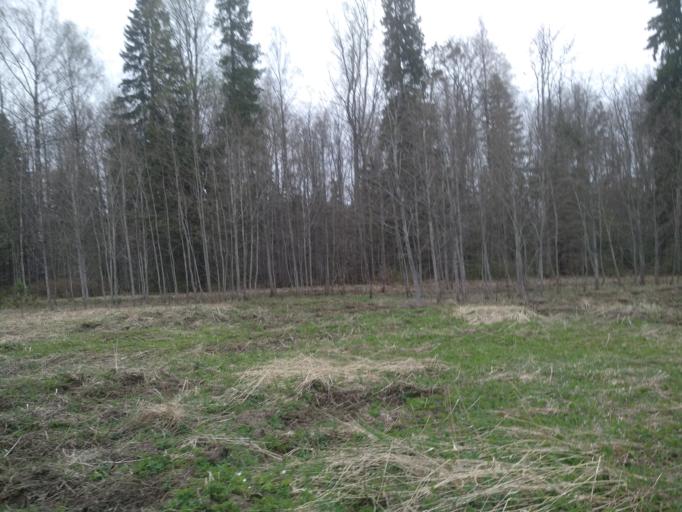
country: RU
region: Leningrad
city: Sosnovo
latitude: 60.4814
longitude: 30.1669
